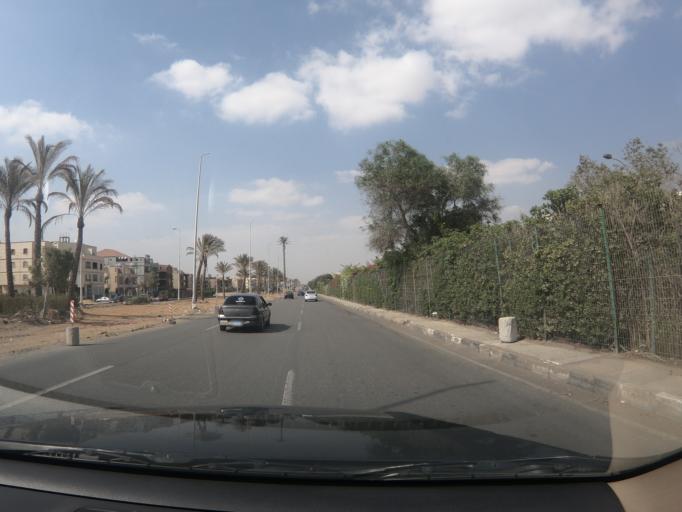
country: EG
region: Muhafazat al Qalyubiyah
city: Al Khankah
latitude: 30.0565
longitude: 31.4751
